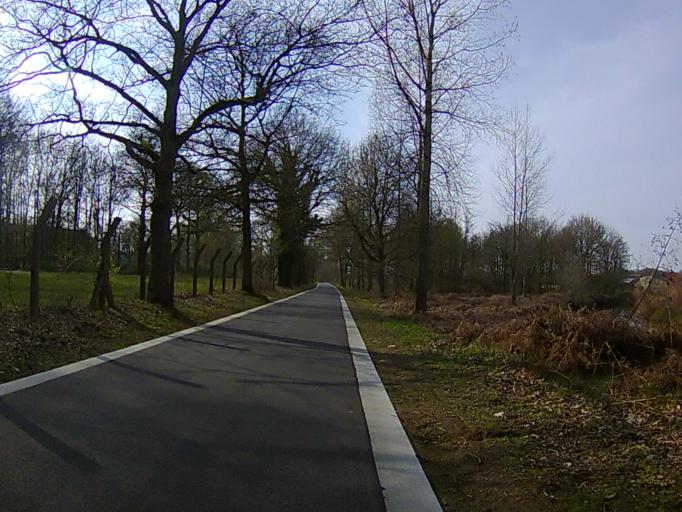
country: BE
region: Flanders
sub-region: Provincie Antwerpen
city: Vorselaar
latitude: 51.1850
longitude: 4.7812
